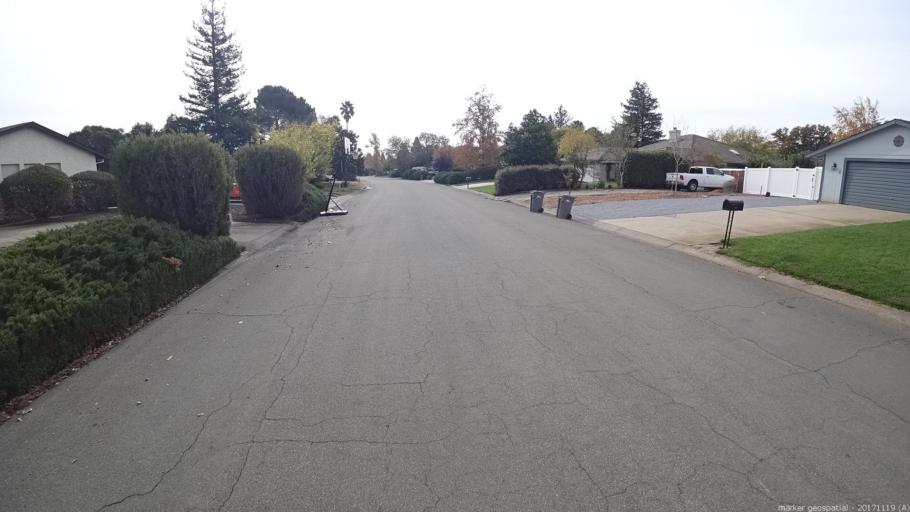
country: US
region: California
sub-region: Shasta County
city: Anderson
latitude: 40.4910
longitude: -122.3079
